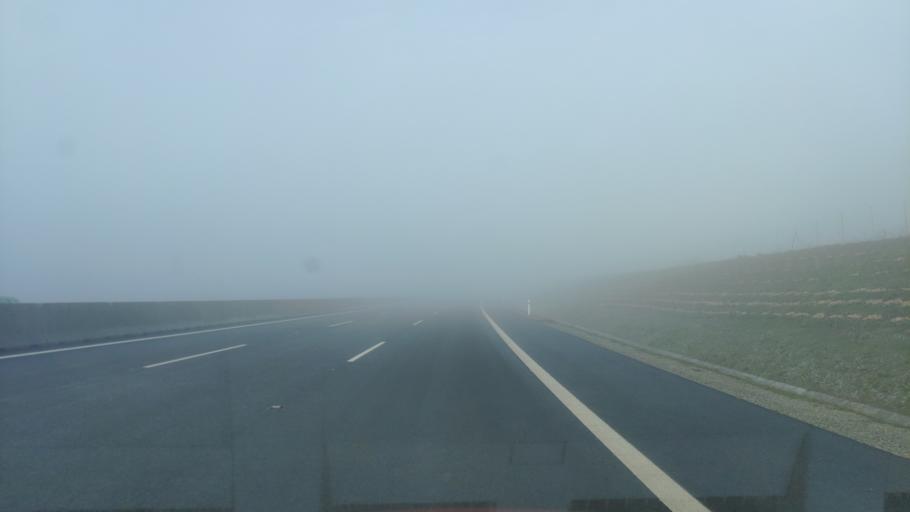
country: SK
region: Kosicky
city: Kosice
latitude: 48.7295
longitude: 21.4090
